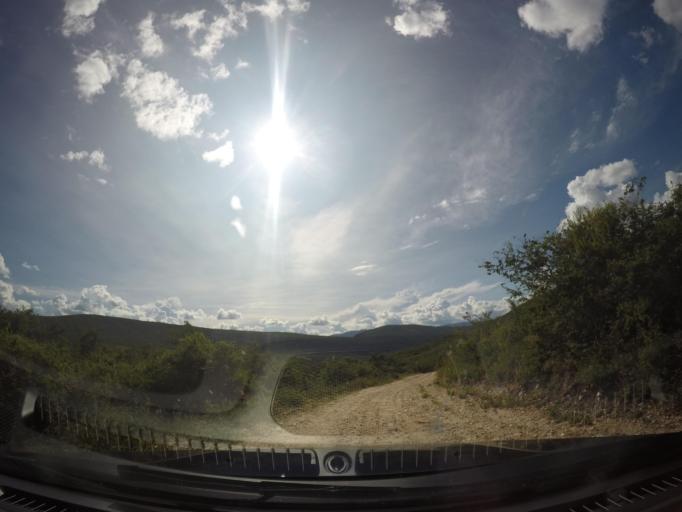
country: BR
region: Bahia
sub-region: Barra Da Estiva
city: Barra da Estiva
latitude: -13.2183
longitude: -41.5952
